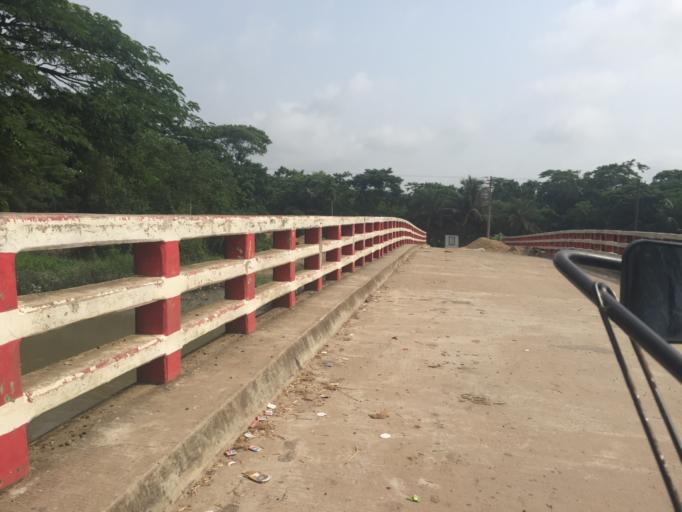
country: BD
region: Barisal
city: Mathba
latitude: 22.2165
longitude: 89.9134
